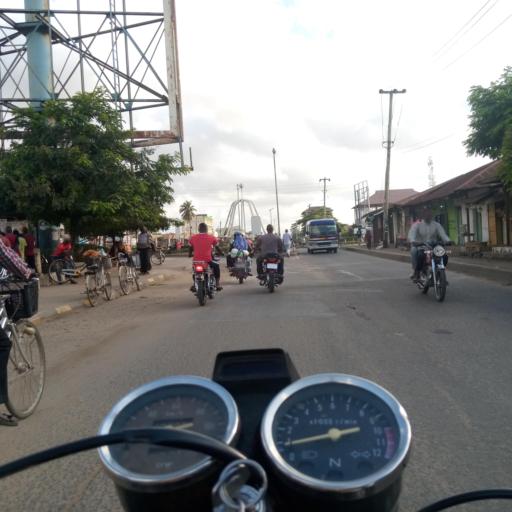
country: TZ
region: Tanga
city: Tanga
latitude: -5.0864
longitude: 39.0972
